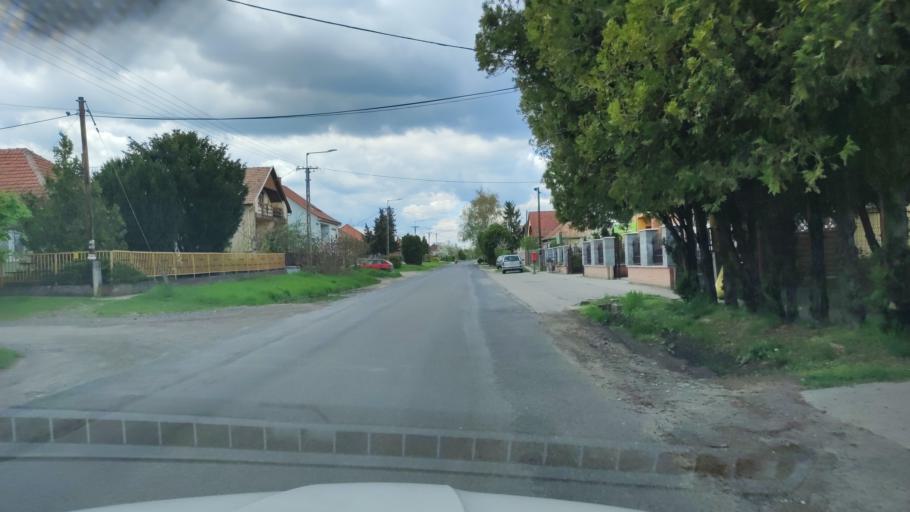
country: HU
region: Pest
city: Cegledbercel
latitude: 47.2114
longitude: 19.7260
